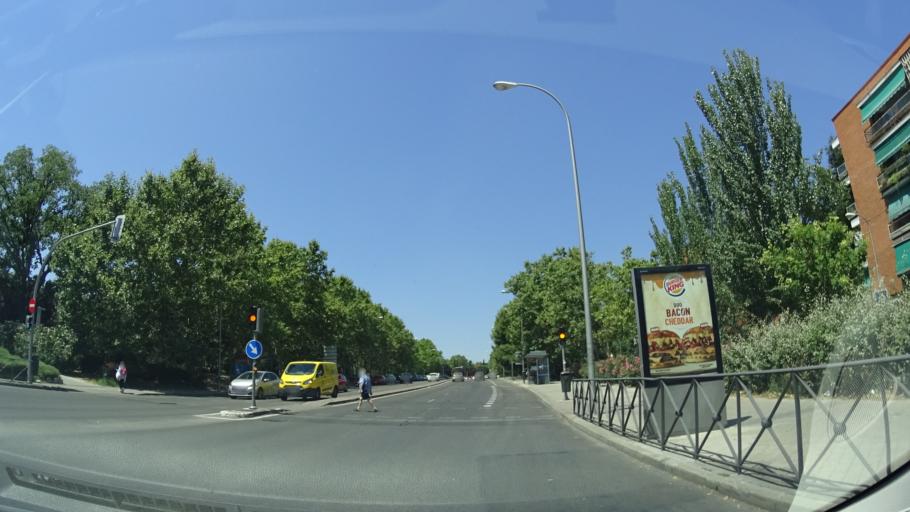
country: ES
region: Madrid
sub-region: Provincia de Madrid
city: Latina
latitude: 40.3765
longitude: -3.7504
